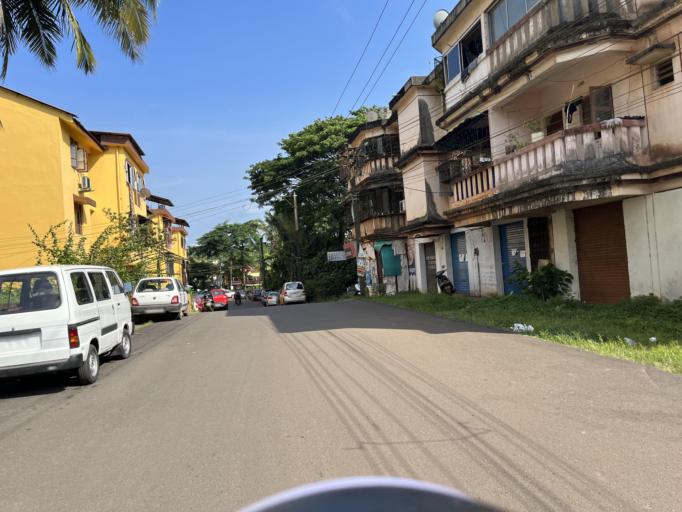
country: IN
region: Goa
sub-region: North Goa
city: Ponda
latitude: 15.3986
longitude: 74.0101
